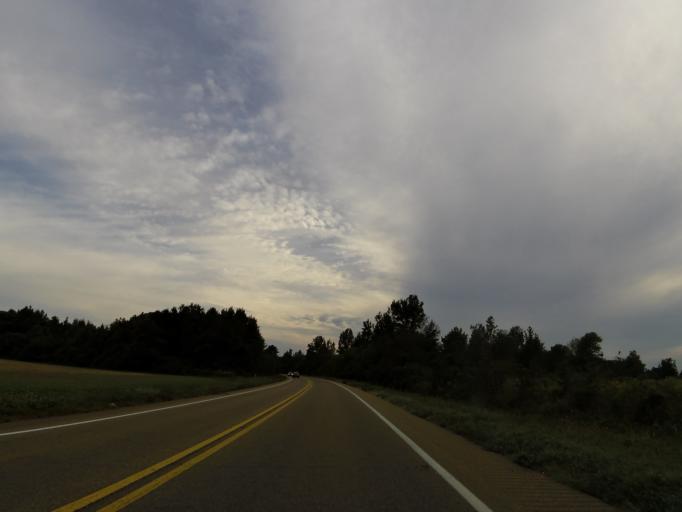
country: US
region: Alabama
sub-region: Monroe County
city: Frisco City
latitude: 31.4166
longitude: -87.4266
